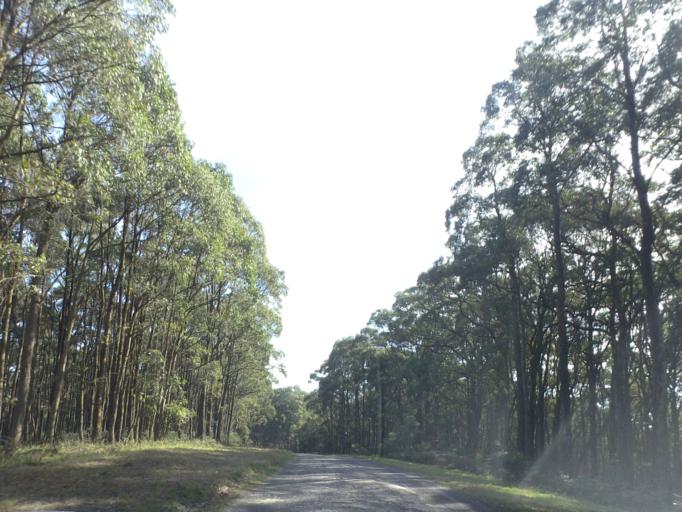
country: AU
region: Victoria
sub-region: Moorabool
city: Bacchus Marsh
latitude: -37.4603
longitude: 144.2156
